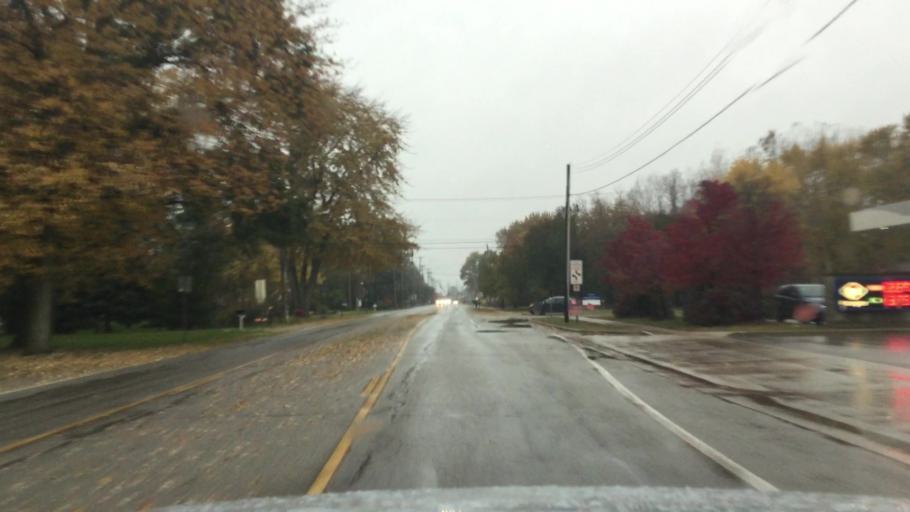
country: US
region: Michigan
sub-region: Saint Clair County
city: Algonac
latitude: 42.6169
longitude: -82.5506
